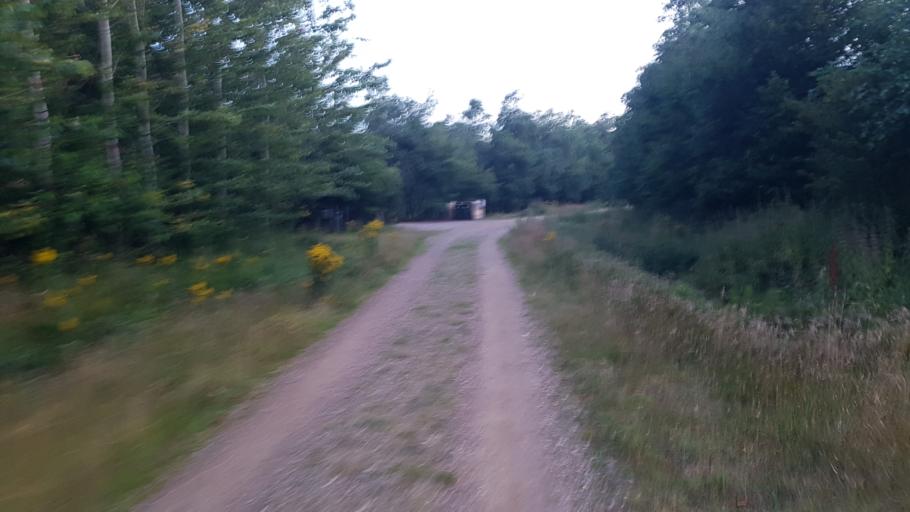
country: DE
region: Schleswig-Holstein
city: List
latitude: 55.0924
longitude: 8.5344
